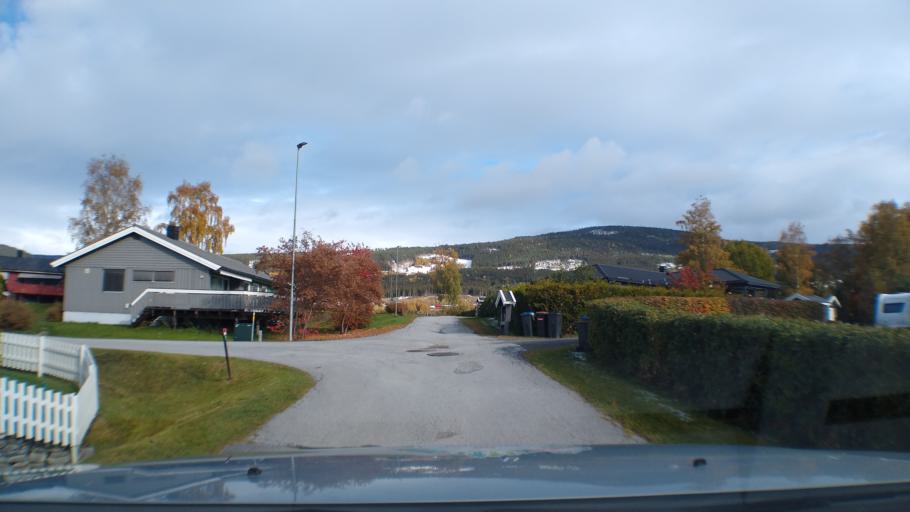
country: NO
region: Oppland
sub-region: Ringebu
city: Ringebu
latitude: 61.5395
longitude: 10.1284
